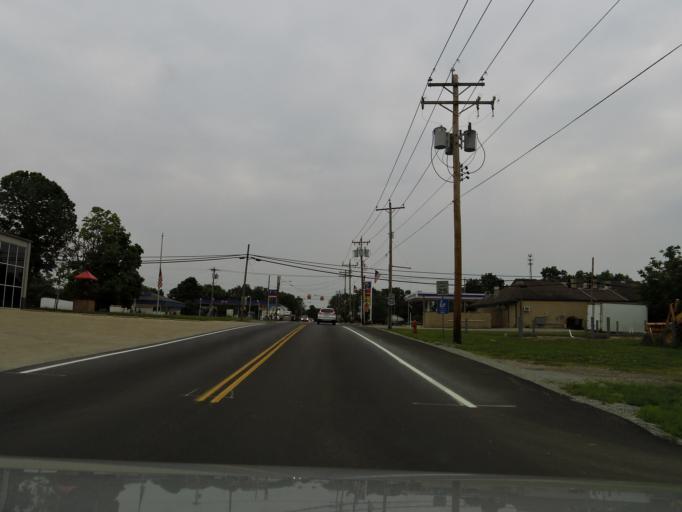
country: US
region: Ohio
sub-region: Clinton County
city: Blanchester
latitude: 39.1876
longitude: -83.9328
